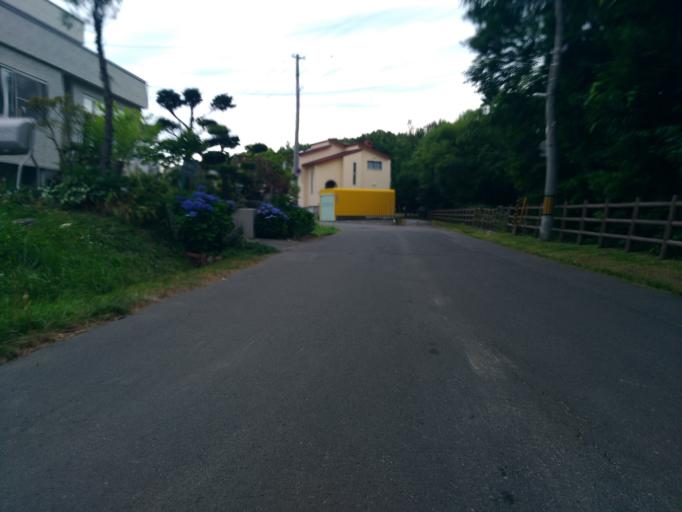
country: JP
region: Hokkaido
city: Ebetsu
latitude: 43.0655
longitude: 141.4993
